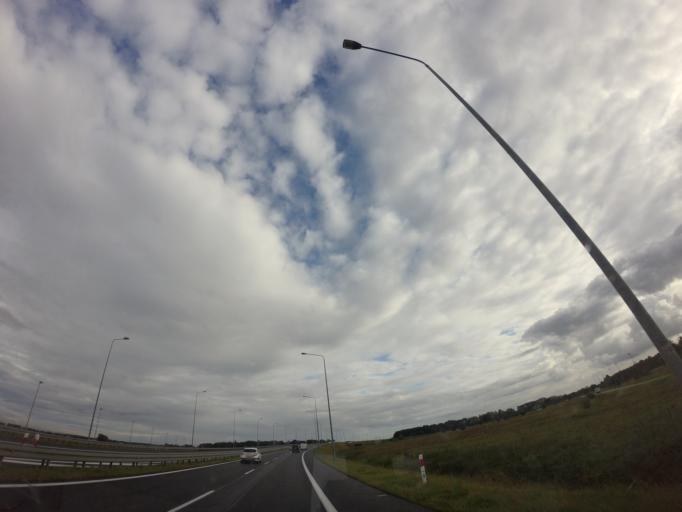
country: PL
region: West Pomeranian Voivodeship
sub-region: Powiat stargardzki
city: Kobylanka
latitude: 53.3515
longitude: 14.9471
